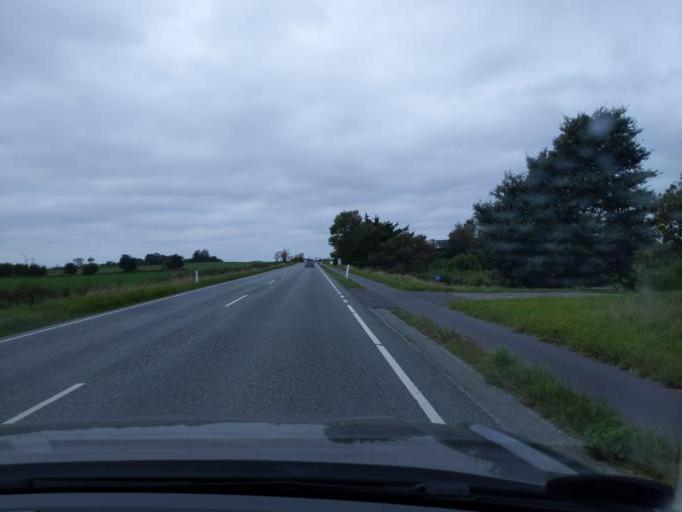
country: DK
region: Central Jutland
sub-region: Randers Kommune
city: Randers
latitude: 56.4982
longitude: 9.9686
